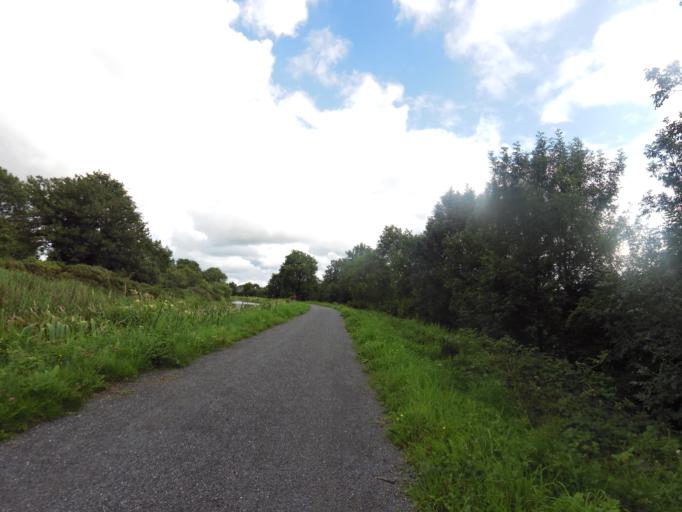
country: IE
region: Leinster
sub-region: An Iarmhi
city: An Muileann gCearr
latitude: 53.5091
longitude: -7.4214
